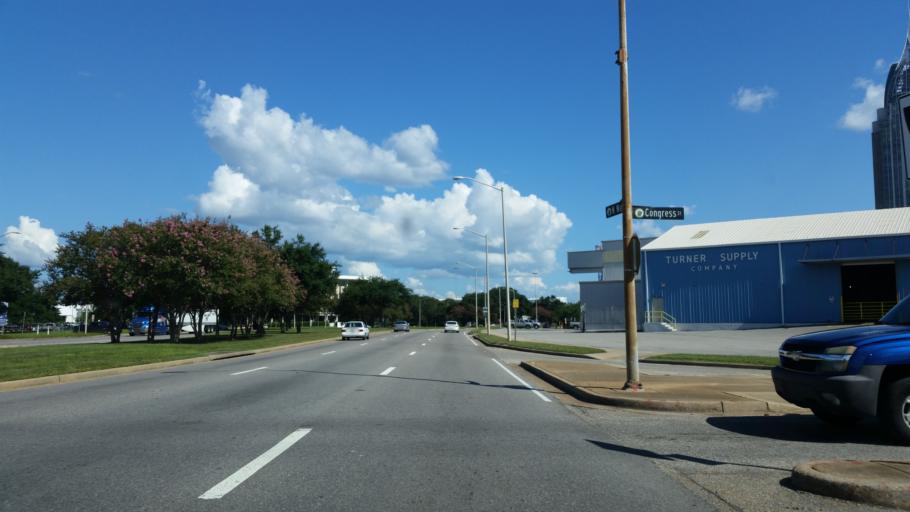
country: US
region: Alabama
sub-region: Mobile County
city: Mobile
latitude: 30.6981
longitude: -88.0428
